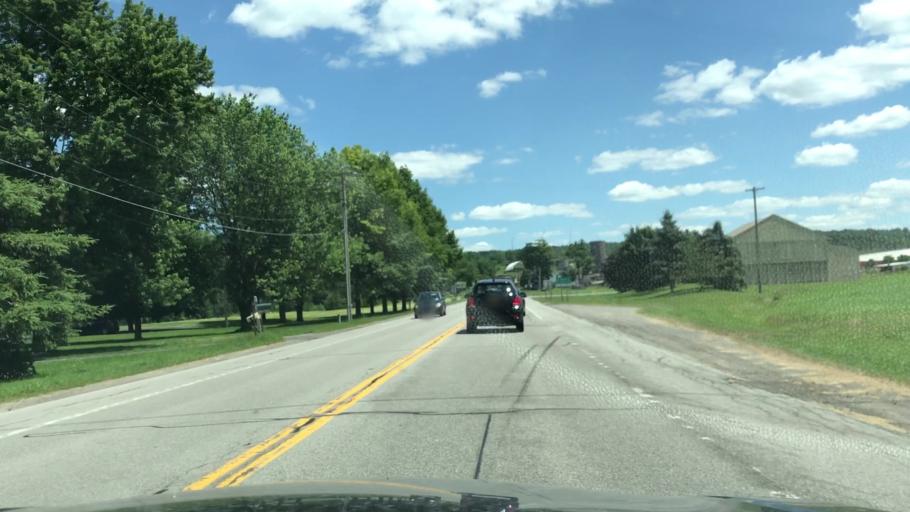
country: US
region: New York
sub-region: Wyoming County
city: Attica
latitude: 42.7572
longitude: -78.3070
